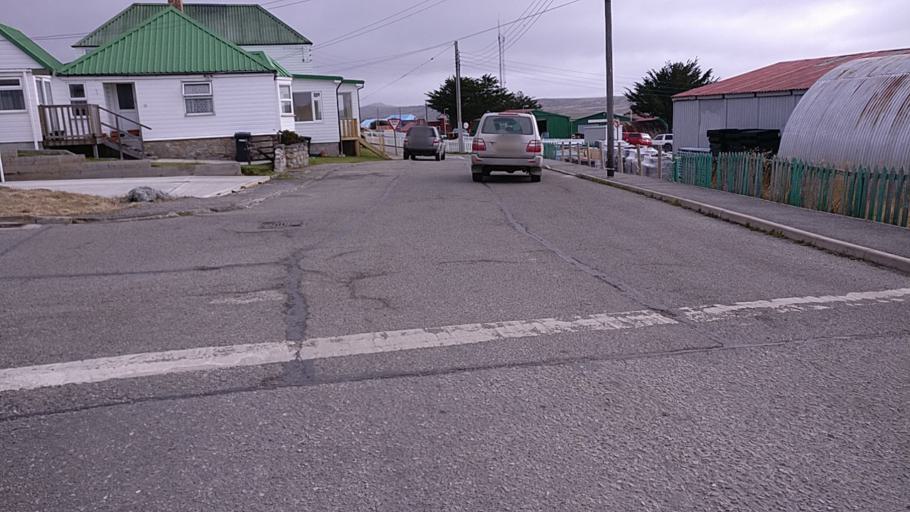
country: FK
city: Stanley
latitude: -51.6930
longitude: -57.8642
